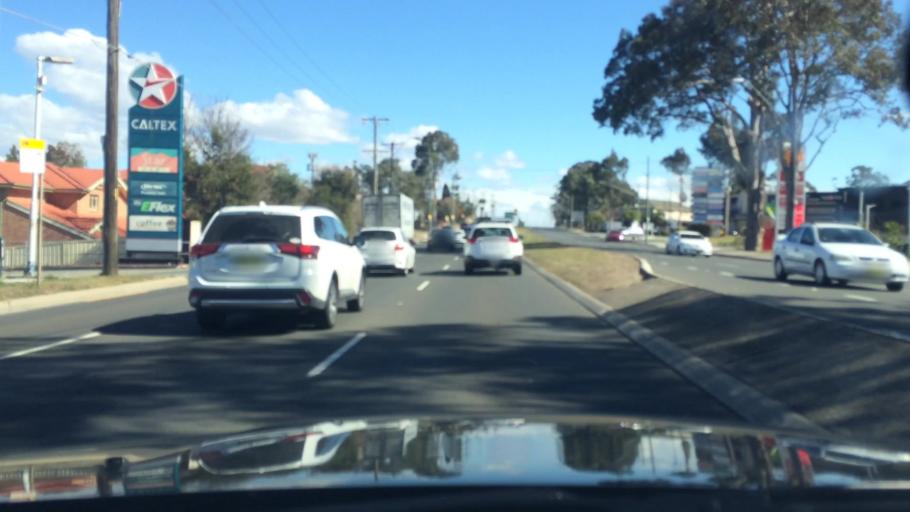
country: AU
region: New South Wales
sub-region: Campbelltown Municipality
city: Glenfield
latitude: -33.9561
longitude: 150.8934
